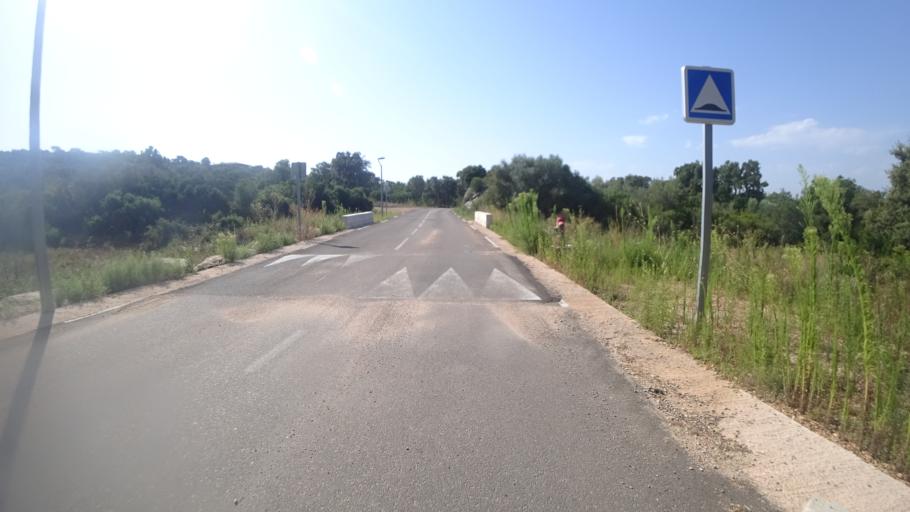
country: FR
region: Corsica
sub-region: Departement de la Corse-du-Sud
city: Porto-Vecchio
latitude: 41.6577
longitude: 9.3253
